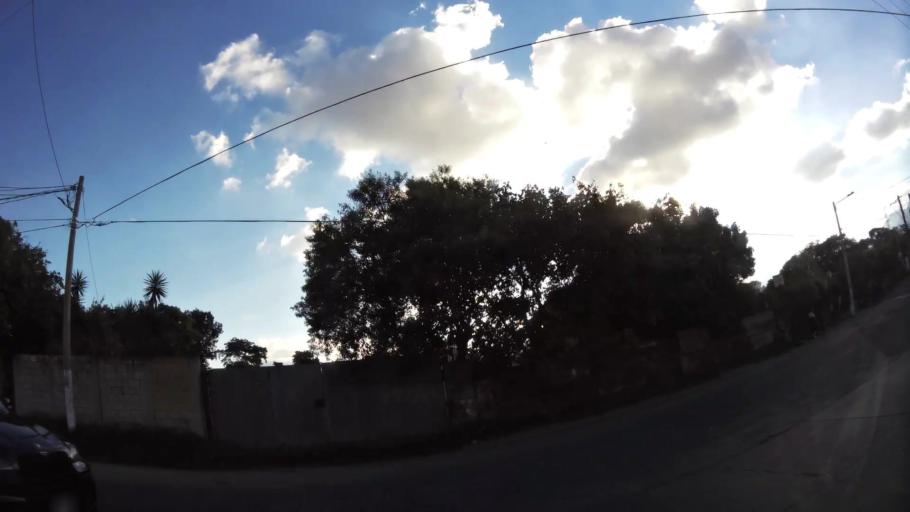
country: GT
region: Guatemala
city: Villa Nueva
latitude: 14.5259
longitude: -90.5826
